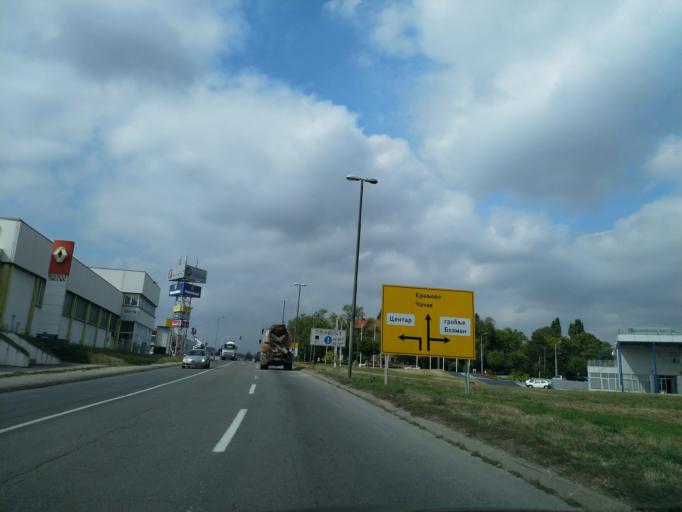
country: RS
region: Central Serbia
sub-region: Sumadijski Okrug
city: Kragujevac
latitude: 44.0240
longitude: 20.9298
